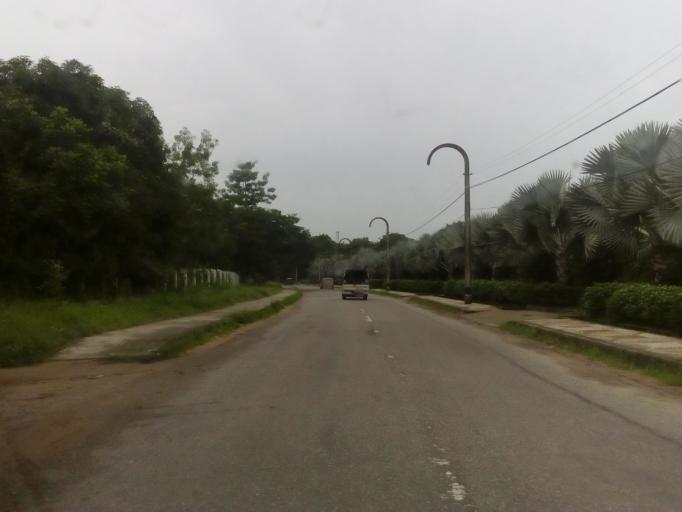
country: MM
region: Yangon
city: Yangon
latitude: 16.8560
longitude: 96.1302
